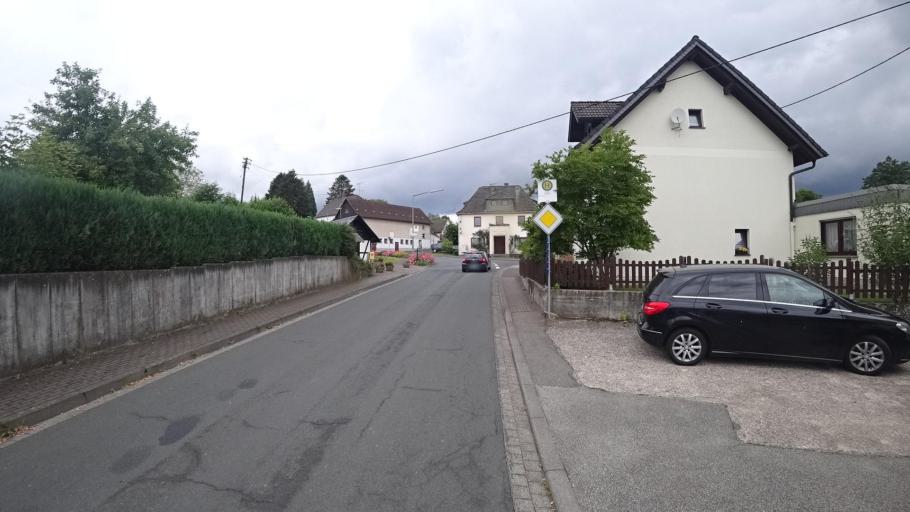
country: DE
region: Rheinland-Pfalz
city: Fiersbach
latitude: 50.6958
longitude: 7.4977
